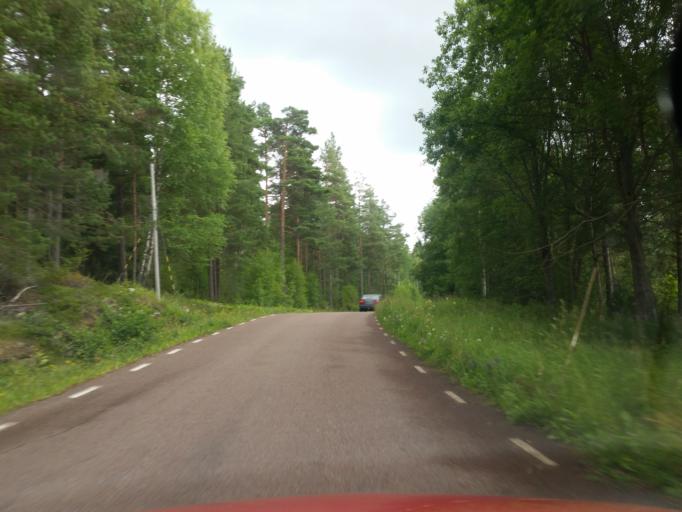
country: SE
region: Dalarna
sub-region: Leksand Municipality
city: Smedby
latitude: 60.6938
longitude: 15.1614
